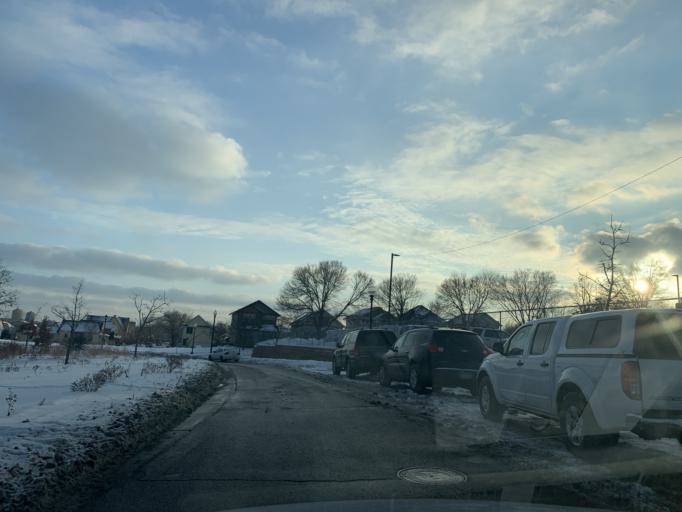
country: US
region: Minnesota
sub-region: Hennepin County
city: Minneapolis
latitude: 44.9907
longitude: -93.2942
